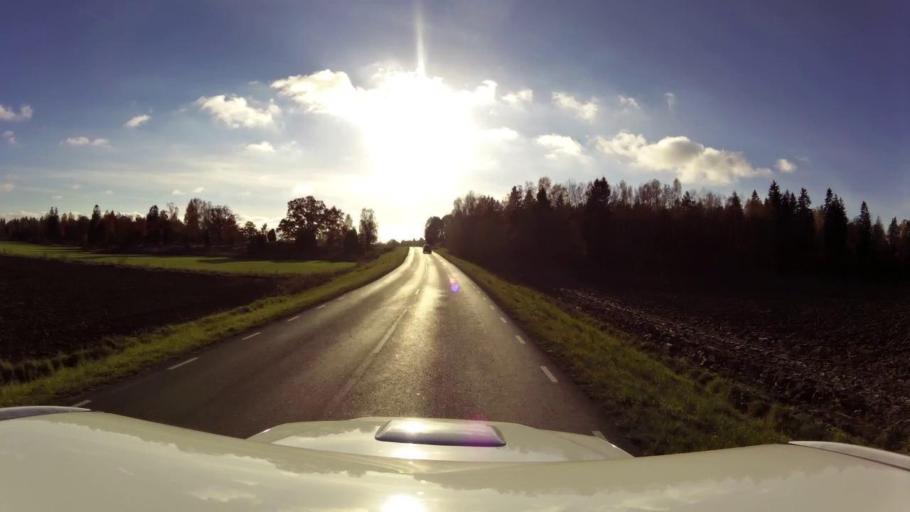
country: SE
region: OEstergoetland
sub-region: Linkopings Kommun
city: Malmslatt
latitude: 58.3411
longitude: 15.5165
